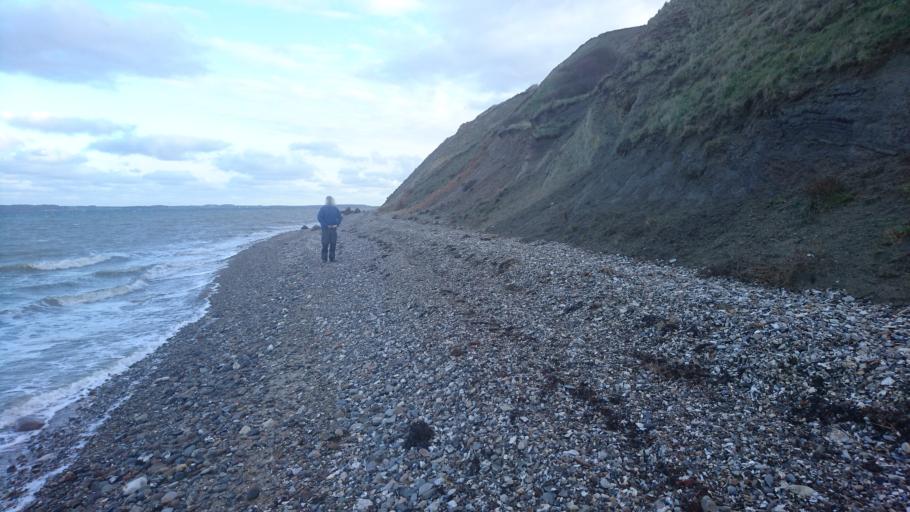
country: DK
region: North Denmark
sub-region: Thisted Kommune
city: Thisted
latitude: 56.8940
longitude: 8.7487
